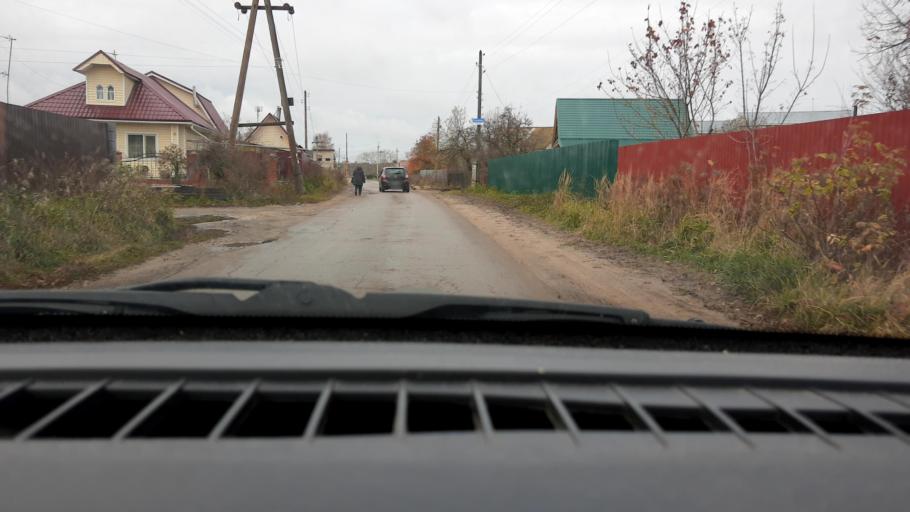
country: RU
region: Nizjnij Novgorod
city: Lukino
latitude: 56.4043
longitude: 43.7224
